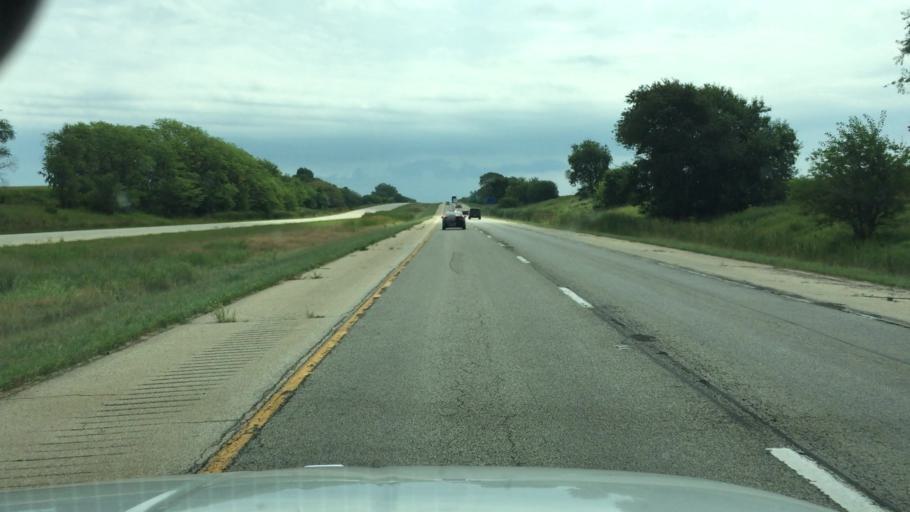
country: US
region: Illinois
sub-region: Peoria County
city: Elmwood
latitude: 40.8390
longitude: -89.9003
